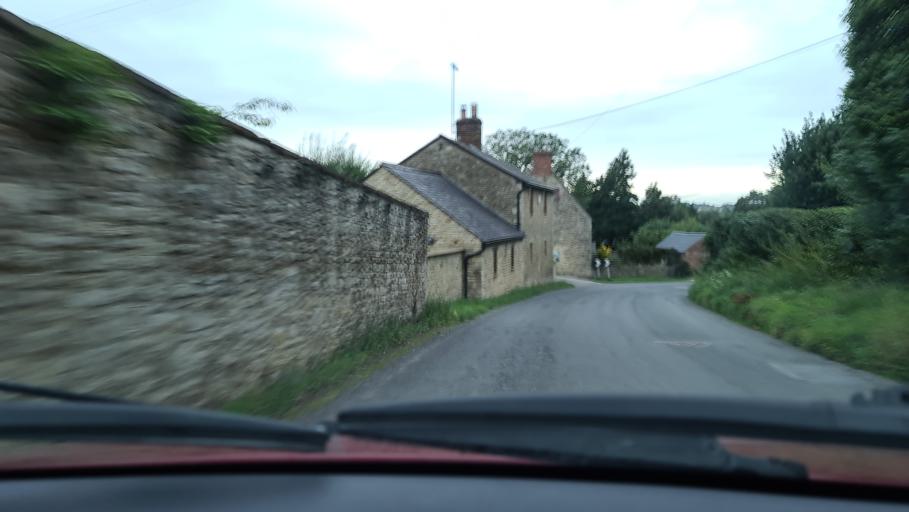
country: GB
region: England
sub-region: Oxfordshire
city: Somerton
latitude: 51.9553
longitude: -1.2771
